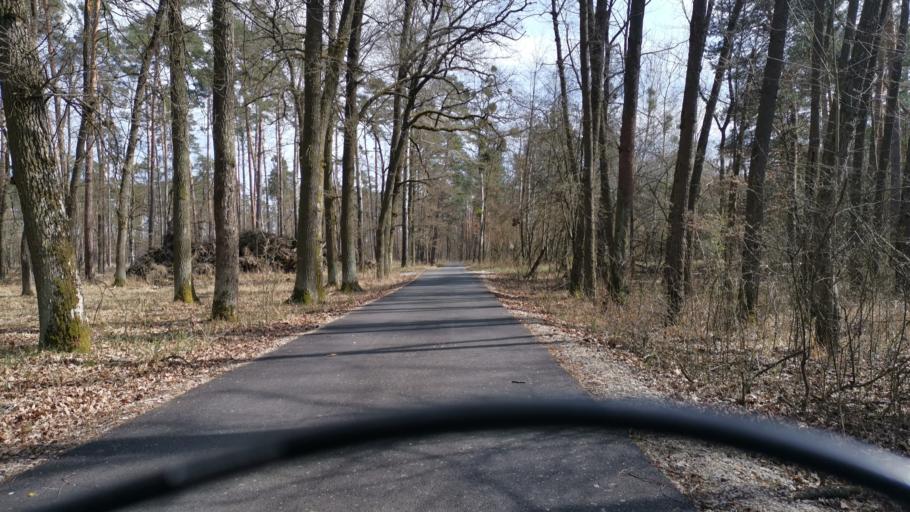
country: SK
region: Trnavsky
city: Gbely
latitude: 48.7101
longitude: 17.0665
